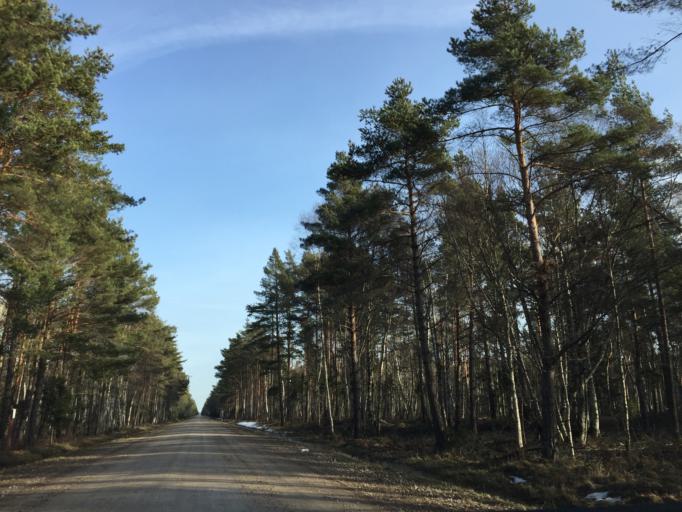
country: EE
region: Saare
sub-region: Kuressaare linn
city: Kuressaare
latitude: 58.2909
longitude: 21.9377
